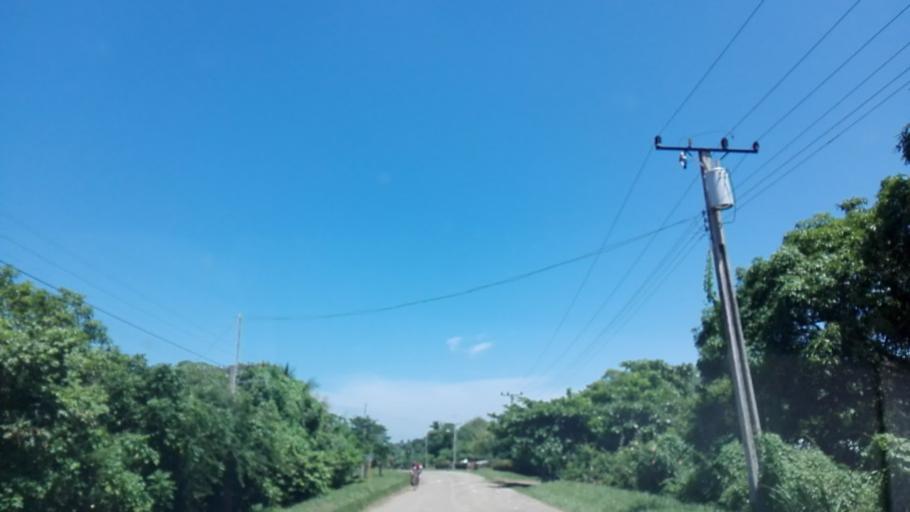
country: CU
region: Granma
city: Bartolome Maso
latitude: 20.1481
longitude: -76.9460
